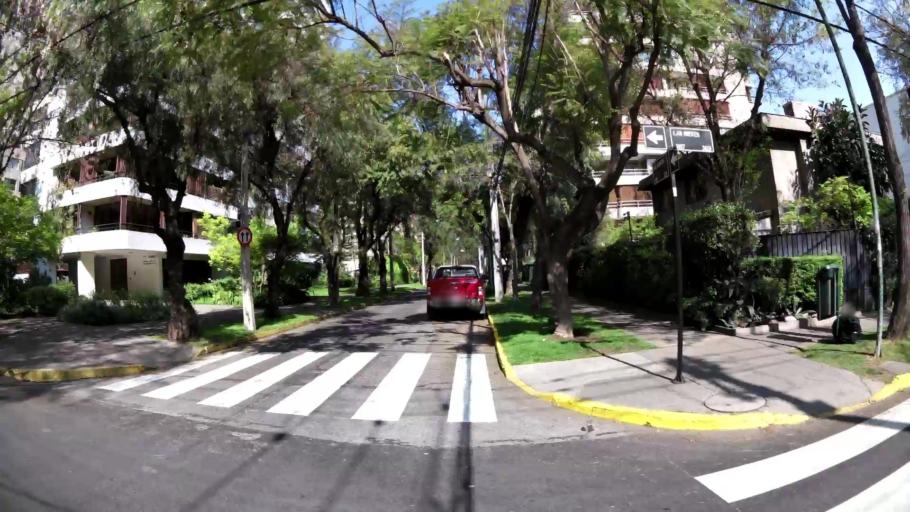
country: CL
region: Santiago Metropolitan
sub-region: Provincia de Santiago
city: Villa Presidente Frei, Nunoa, Santiago, Chile
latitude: -33.4042
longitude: -70.5936
